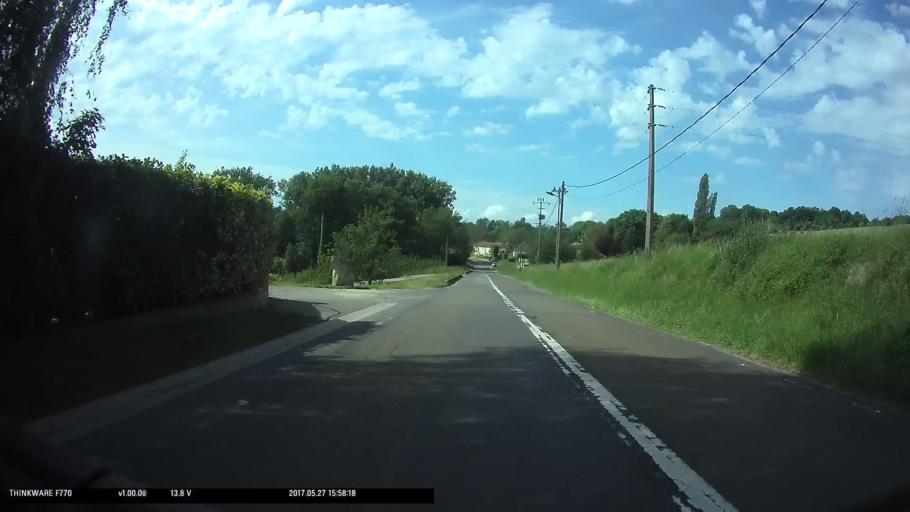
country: FR
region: Ile-de-France
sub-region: Departement du Val-d'Oise
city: Us
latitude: 49.0992
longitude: 1.9765
